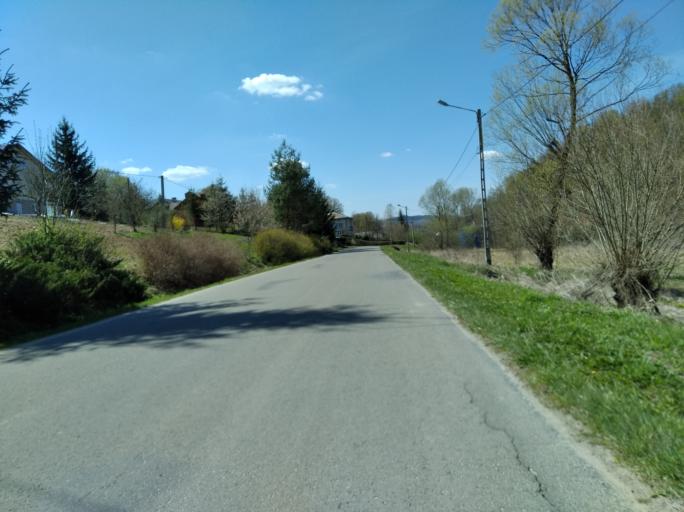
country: PL
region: Subcarpathian Voivodeship
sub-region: Powiat brzozowski
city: Golcowa
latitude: 49.7684
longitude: 22.0439
